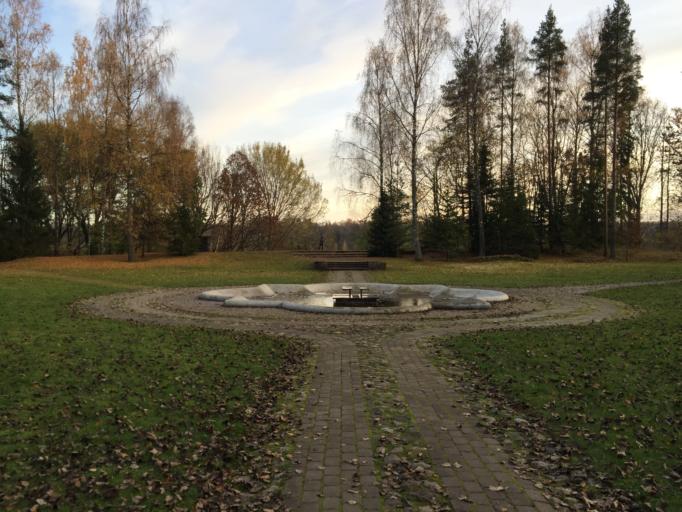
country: LV
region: Jaunjelgava
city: Jaunjelgava
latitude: 56.6163
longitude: 25.0550
